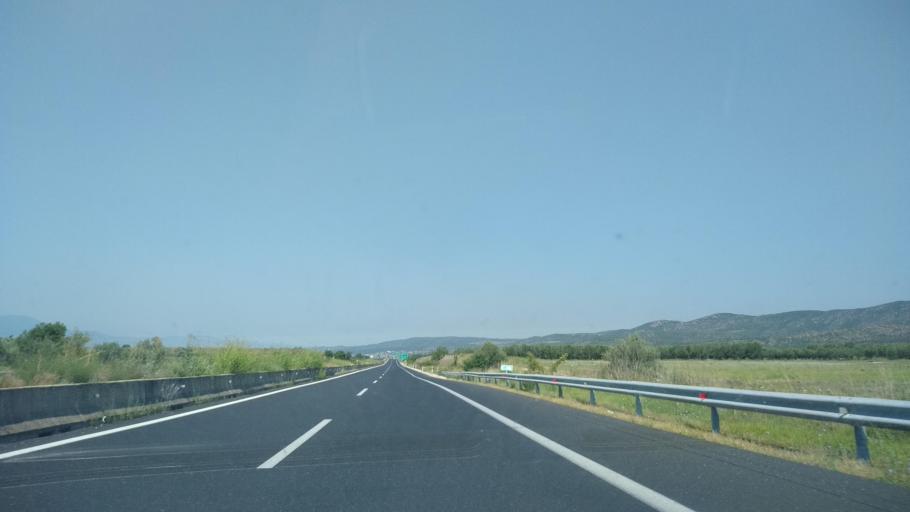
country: GR
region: Central Macedonia
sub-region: Nomos Thessalonikis
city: Askos
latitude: 40.7008
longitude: 23.3929
